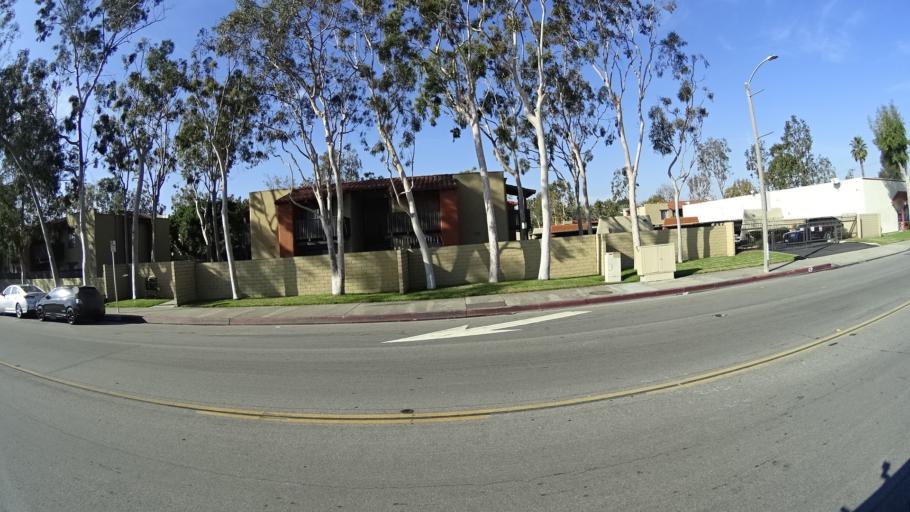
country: US
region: California
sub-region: Orange County
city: Midway City
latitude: 33.7294
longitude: -117.9808
